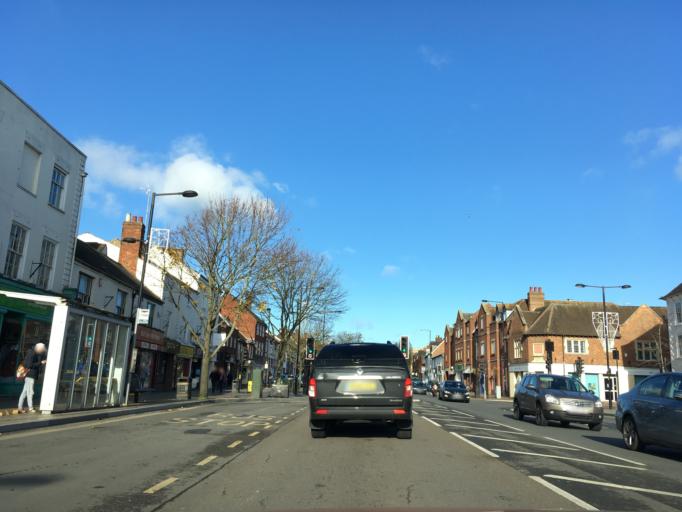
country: GB
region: England
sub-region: Worcestershire
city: Evesham
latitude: 52.0940
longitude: -1.9469
